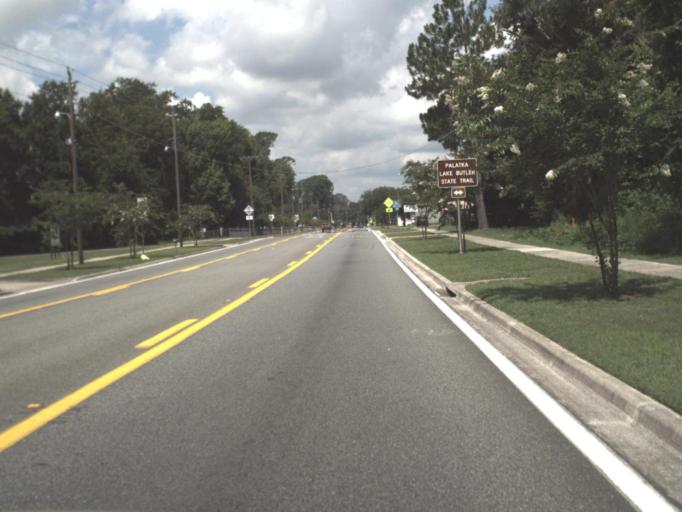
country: US
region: Florida
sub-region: Union County
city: Lake Butler
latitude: 30.0184
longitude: -82.3328
